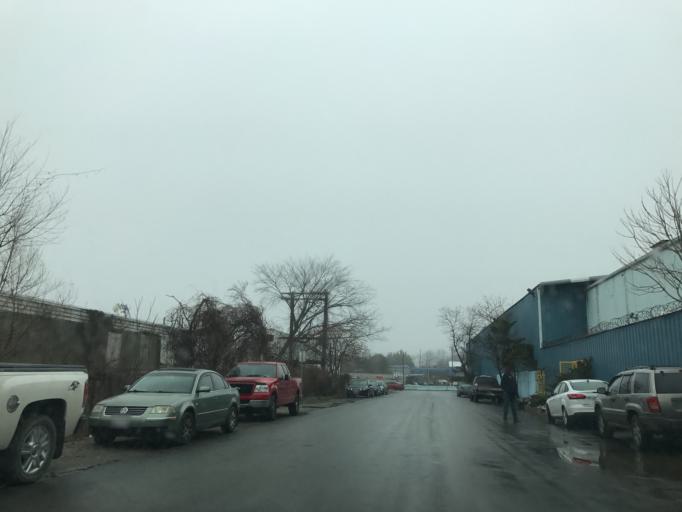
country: US
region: Maryland
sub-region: Baltimore County
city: Dundalk
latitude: 39.2568
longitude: -76.4982
